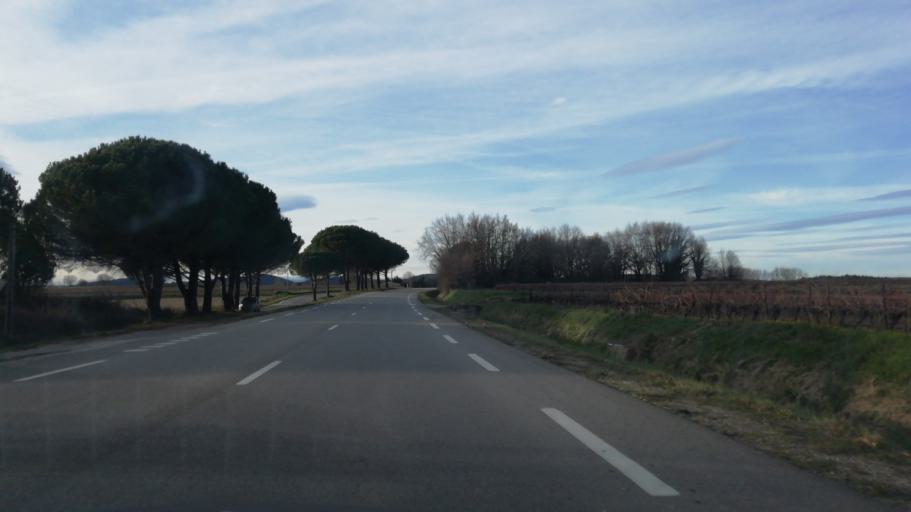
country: FR
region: Languedoc-Roussillon
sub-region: Departement du Gard
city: Saint-Mamert-du-Gard
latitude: 43.8579
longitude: 4.1718
